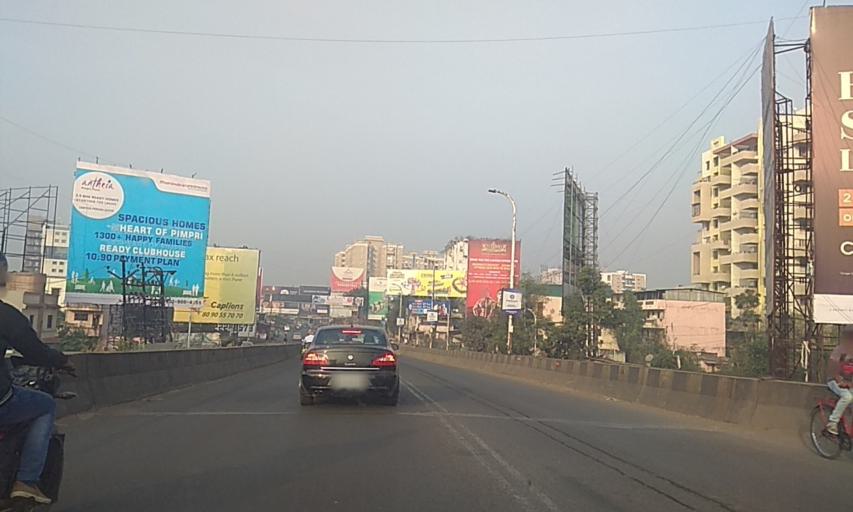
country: IN
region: Maharashtra
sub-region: Pune Division
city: Pimpri
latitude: 18.5920
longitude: 73.7562
